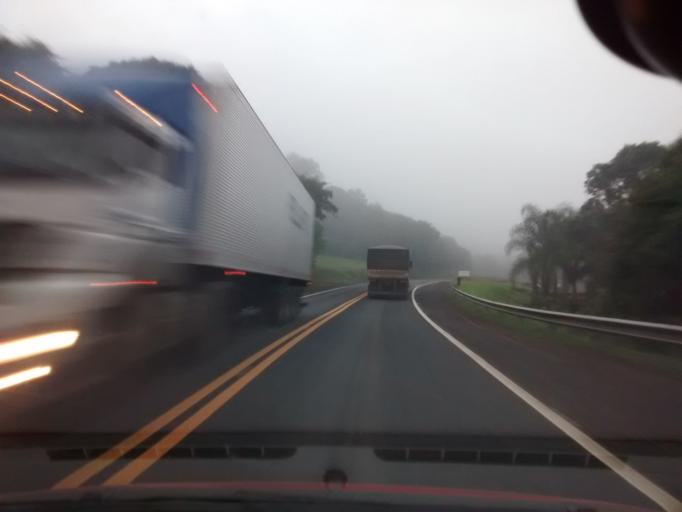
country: BR
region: Rio Grande do Sul
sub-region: Vacaria
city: Estrela
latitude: -28.1962
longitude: -50.7431
